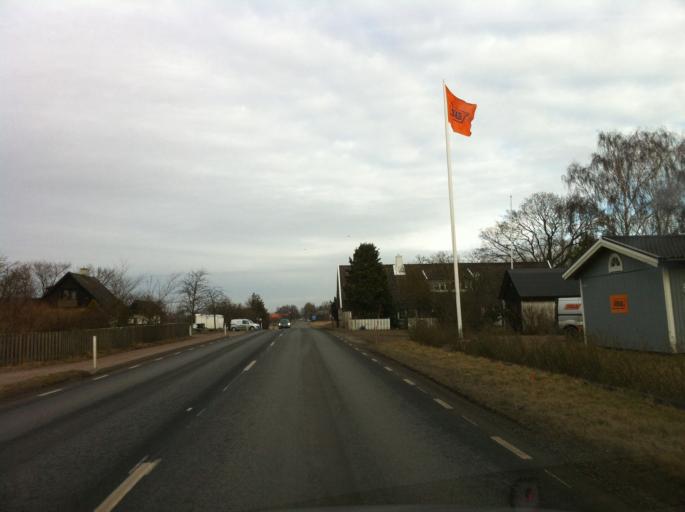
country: SE
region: Skane
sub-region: Angelholms Kommun
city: Strovelstorp
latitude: 56.1884
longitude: 12.8483
